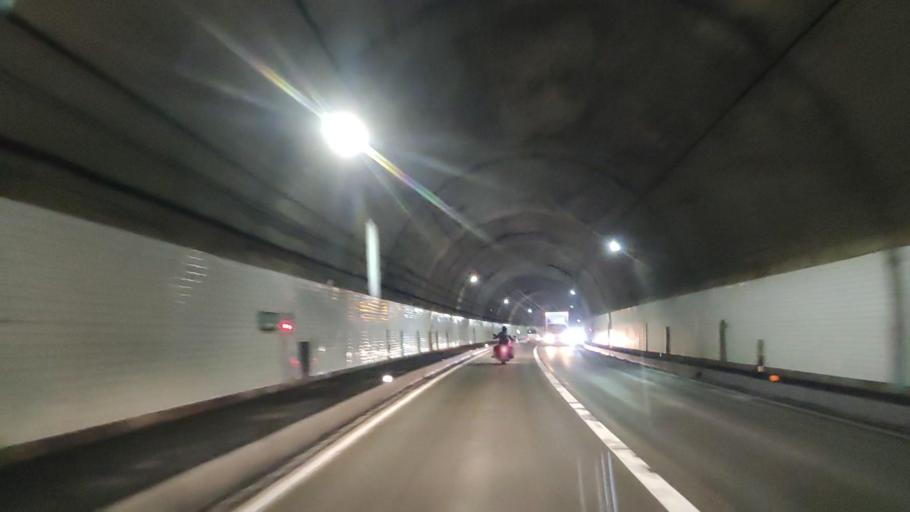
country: JP
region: Akita
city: Yuzawa
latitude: 39.0039
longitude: 140.3698
